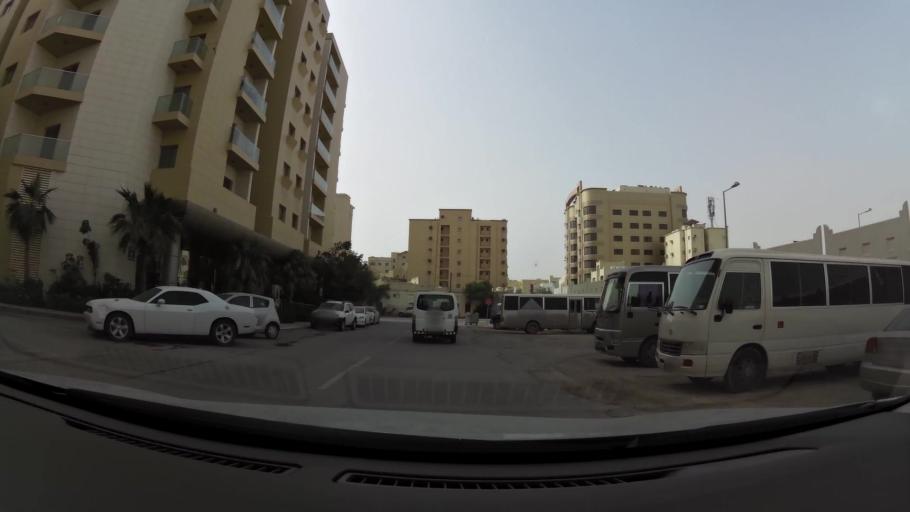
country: QA
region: Baladiyat ad Dawhah
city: Doha
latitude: 25.2794
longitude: 51.5499
